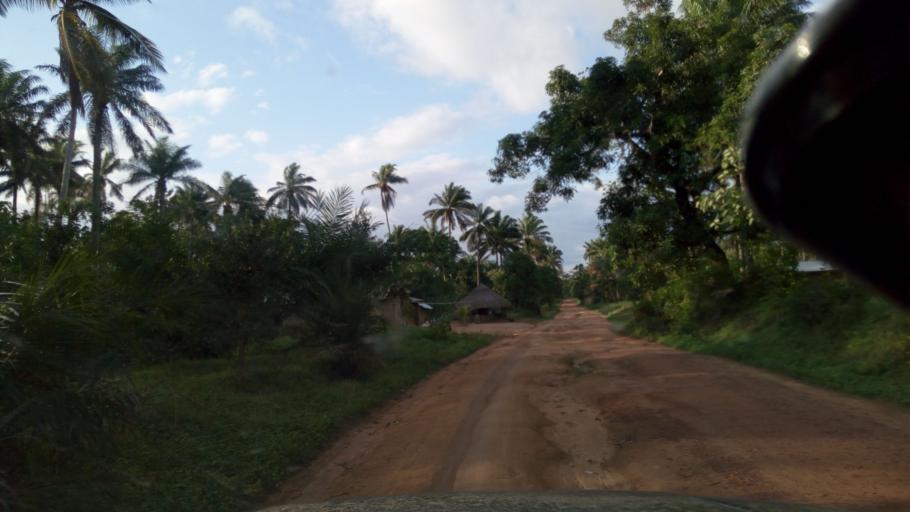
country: SL
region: Northern Province
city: Konakridee
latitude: 8.7712
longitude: -13.1392
